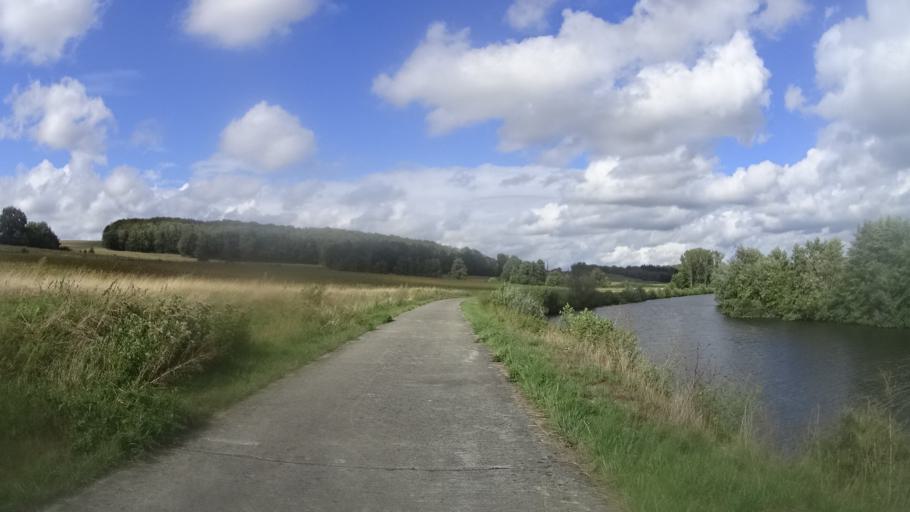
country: BE
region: Wallonia
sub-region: Province du Hainaut
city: Merbes-le-Chateau
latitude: 50.3205
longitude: 4.2038
